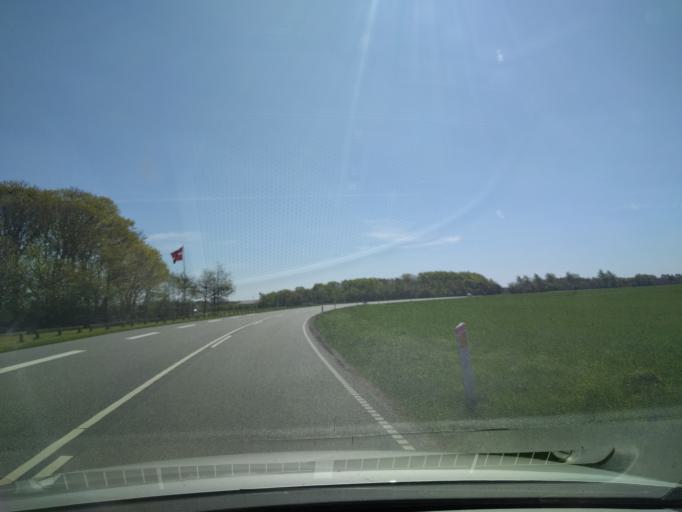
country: DK
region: Central Jutland
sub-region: Ringkobing-Skjern Kommune
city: Tarm
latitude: 55.8854
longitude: 8.5234
